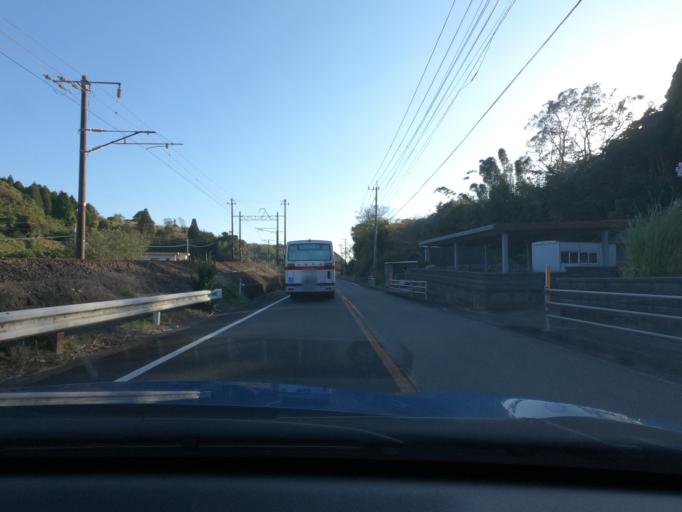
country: JP
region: Kagoshima
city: Akune
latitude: 31.9933
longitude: 130.1976
